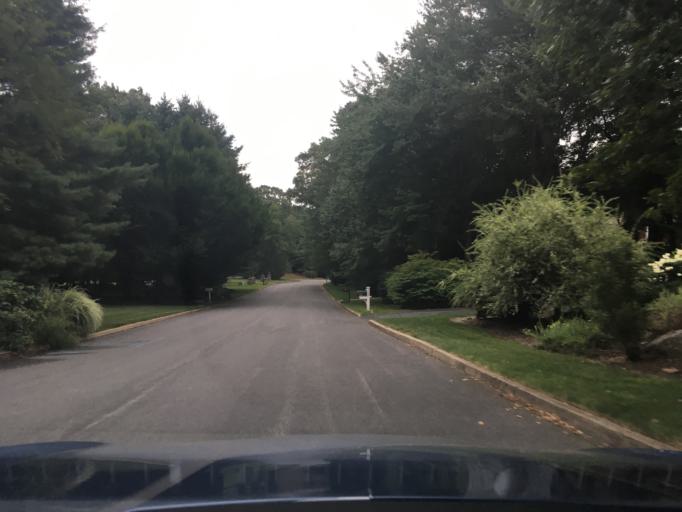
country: US
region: Rhode Island
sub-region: Kent County
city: East Greenwich
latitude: 41.6336
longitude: -71.5017
